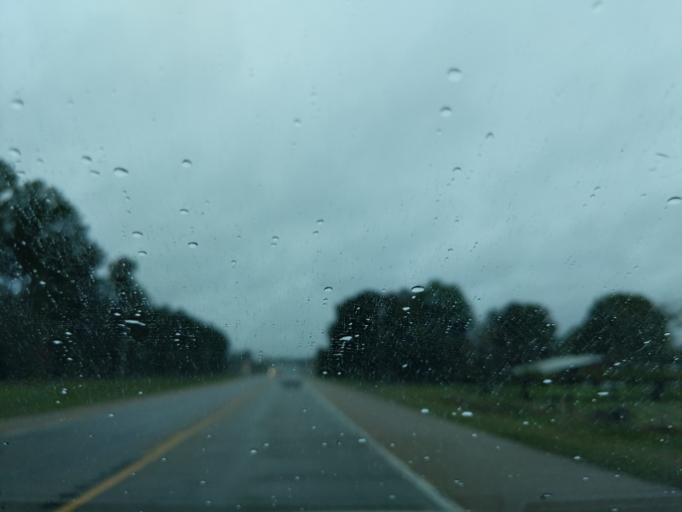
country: US
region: Louisiana
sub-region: Webster Parish
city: Minden
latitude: 32.5888
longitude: -93.2478
